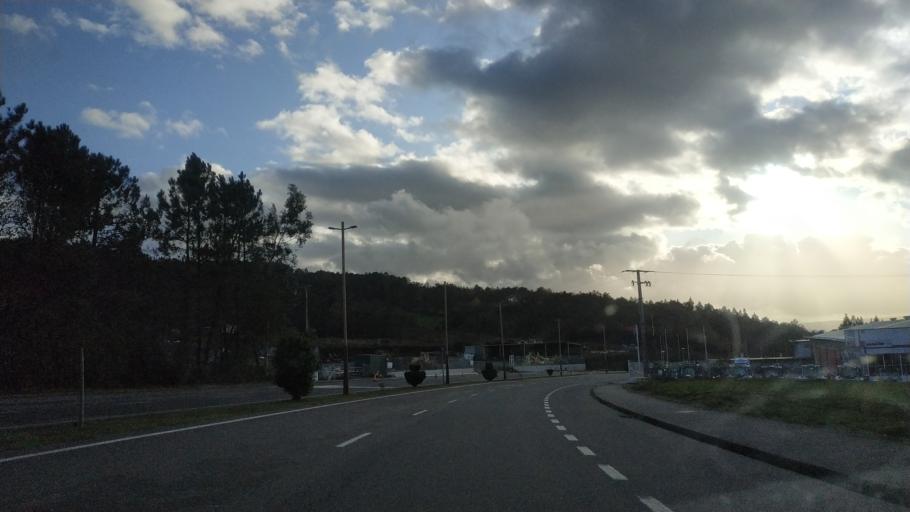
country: ES
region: Galicia
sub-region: Provincia de Pontevedra
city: Silleda
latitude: 42.7914
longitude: -8.1612
